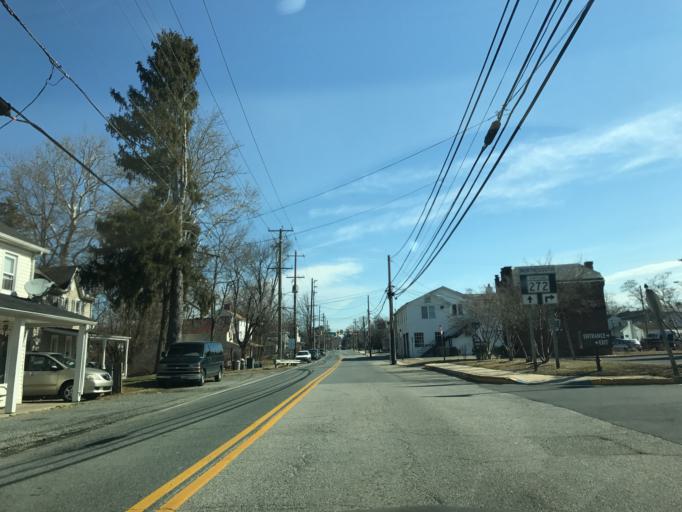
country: US
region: Maryland
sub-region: Cecil County
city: North East
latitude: 39.6010
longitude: -75.9450
